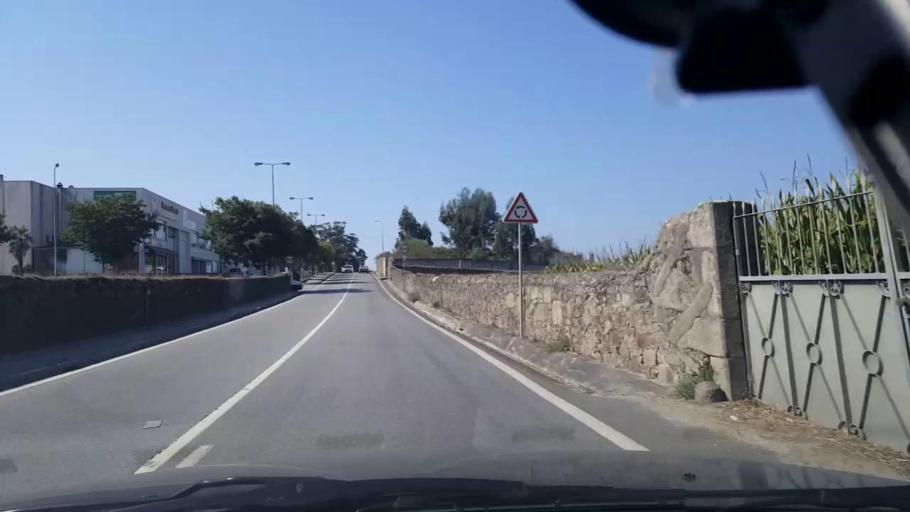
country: PT
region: Porto
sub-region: Povoa de Varzim
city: Pedroso
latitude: 41.3927
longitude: -8.6978
